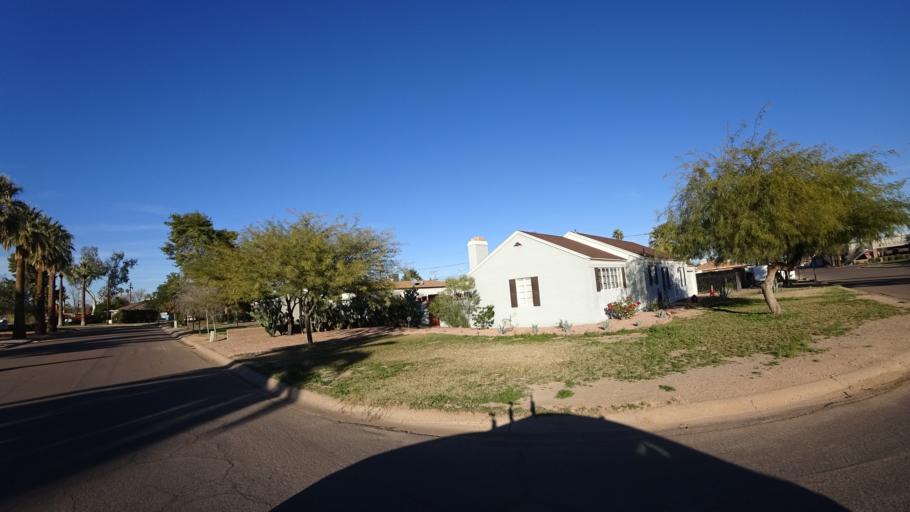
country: US
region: Arizona
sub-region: Maricopa County
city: Phoenix
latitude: 33.4824
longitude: -112.0924
